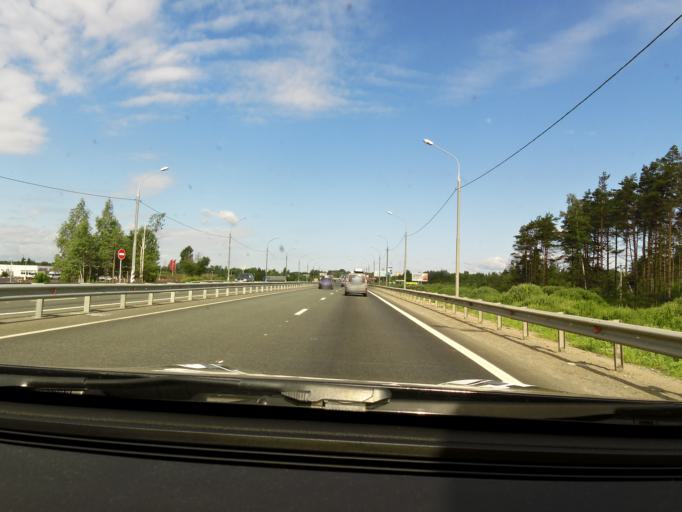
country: RU
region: Tverskaya
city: Emmaus
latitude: 56.7707
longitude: 36.1399
